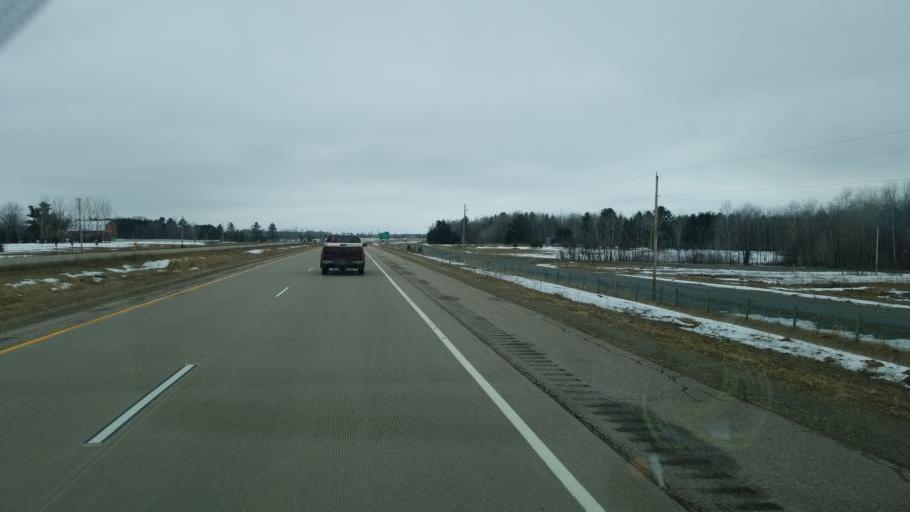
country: US
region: Wisconsin
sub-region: Portage County
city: Stevens Point
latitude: 44.5996
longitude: -89.6868
